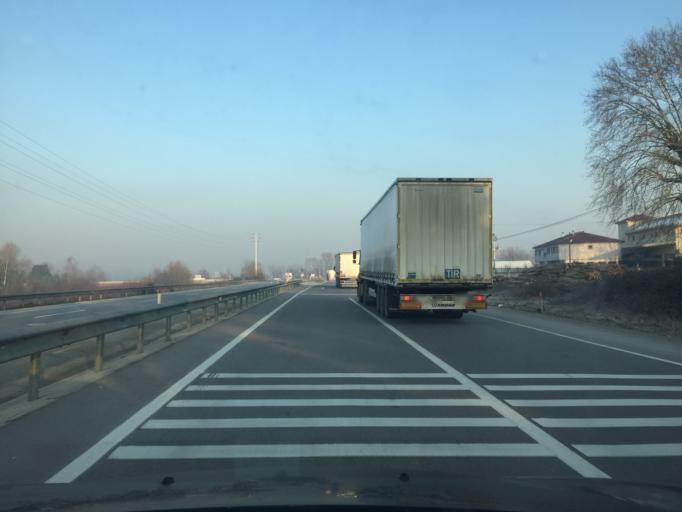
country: TR
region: Sakarya
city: Akyazi
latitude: 40.6715
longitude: 30.5879
